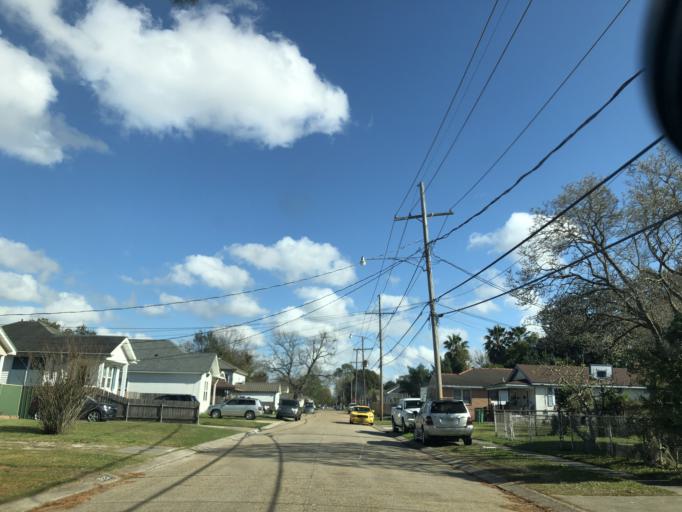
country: US
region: Louisiana
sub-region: Jefferson Parish
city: Metairie Terrace
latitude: 29.9784
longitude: -90.1659
